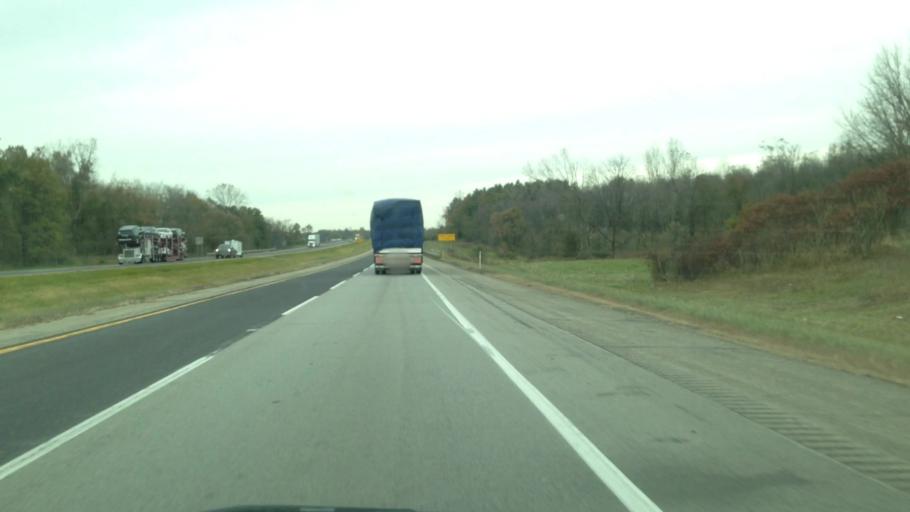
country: US
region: Indiana
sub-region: Steuben County
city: Fremont
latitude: 41.6511
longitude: -84.8432
